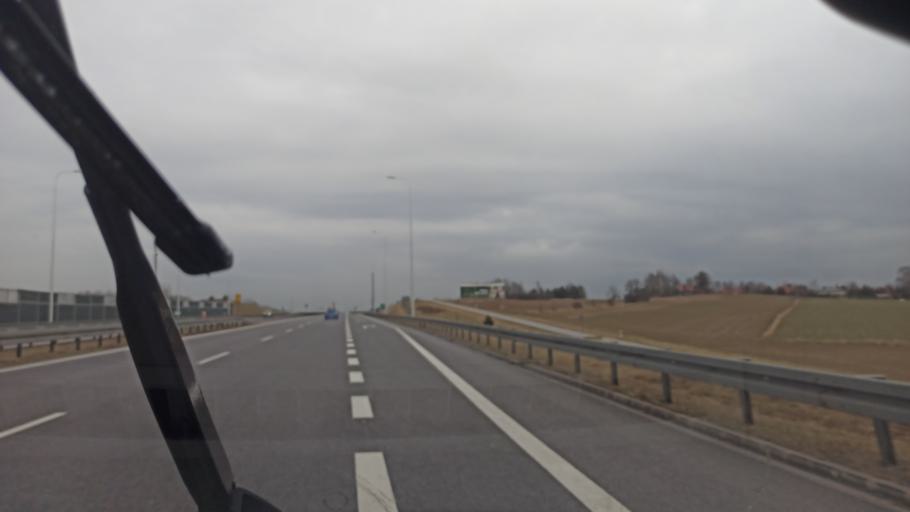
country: PL
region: Lublin Voivodeship
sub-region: Powiat lubelski
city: Jastkow
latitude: 51.2784
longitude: 22.4406
